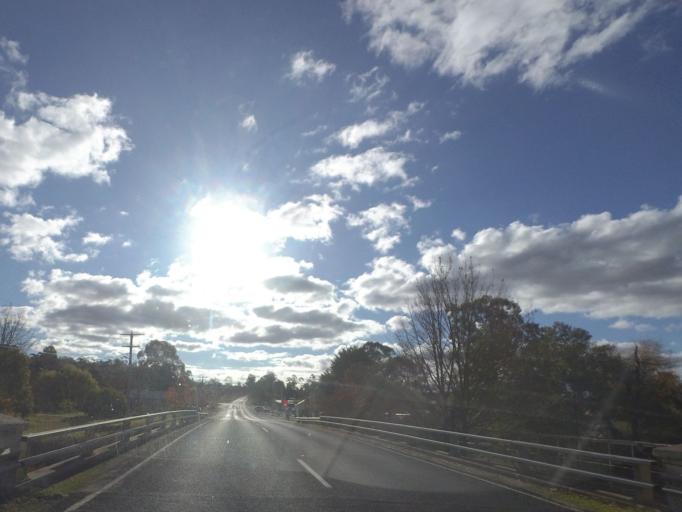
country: AU
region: Victoria
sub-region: Mount Alexander
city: Castlemaine
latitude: -37.1397
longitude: 144.3493
